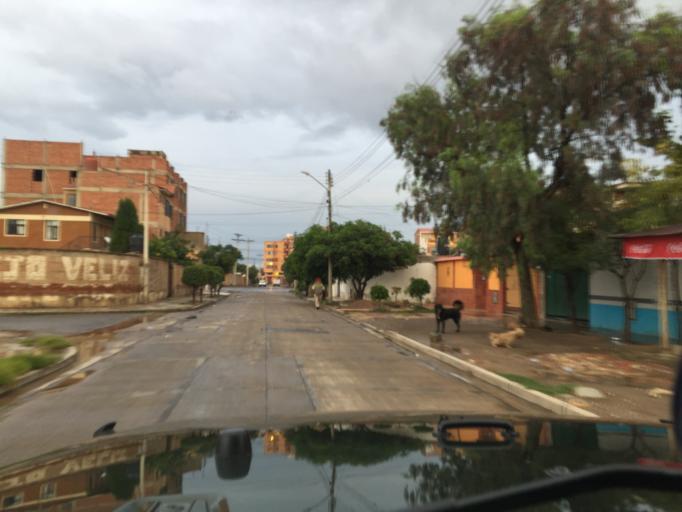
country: BO
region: Cochabamba
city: Cochabamba
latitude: -17.4191
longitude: -66.1652
